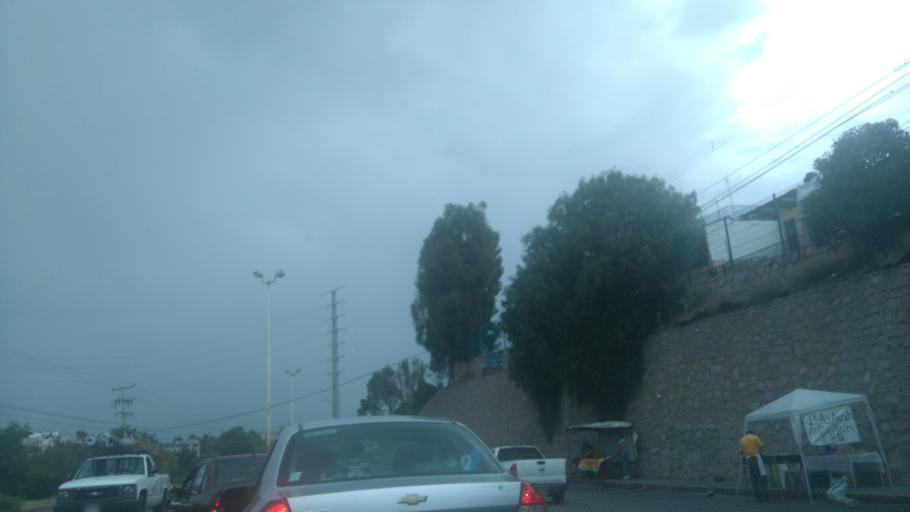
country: MX
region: Zacatecas
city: Zacatecas
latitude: 22.7587
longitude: -102.5871
